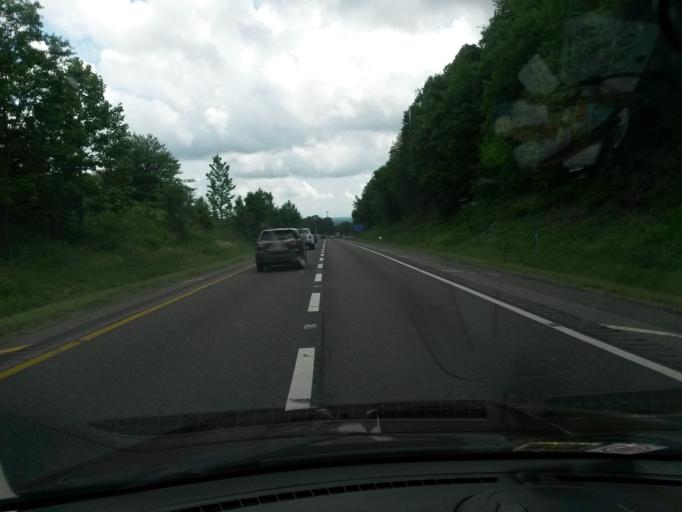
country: US
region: Virginia
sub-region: Carroll County
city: Cana
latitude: 36.5921
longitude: -80.7425
